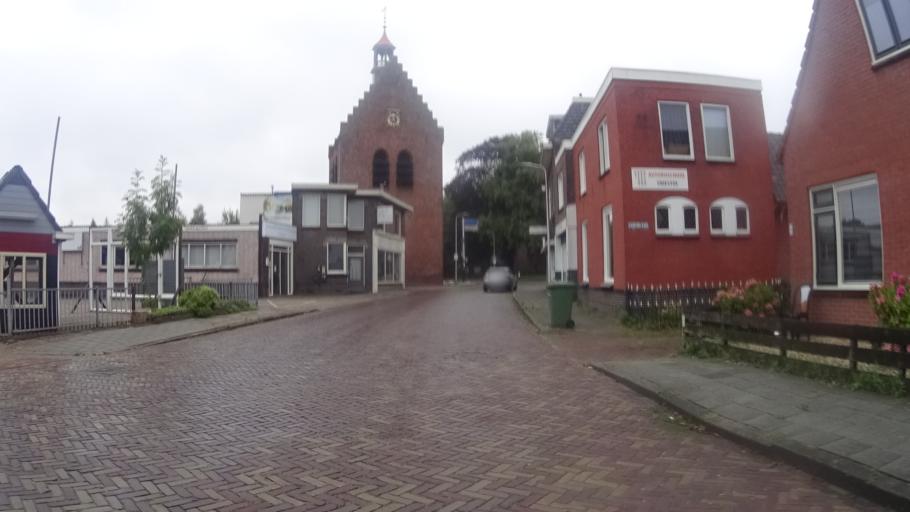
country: NL
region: Groningen
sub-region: Gemeente  Oldambt
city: Winschoten
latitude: 53.1779
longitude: 6.9703
